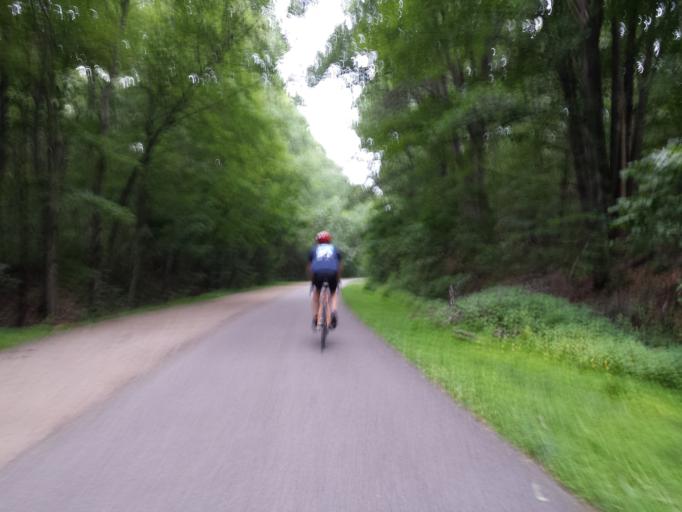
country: US
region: New York
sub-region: Dutchess County
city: Hillside Lake
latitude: 41.5863
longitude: -73.8178
